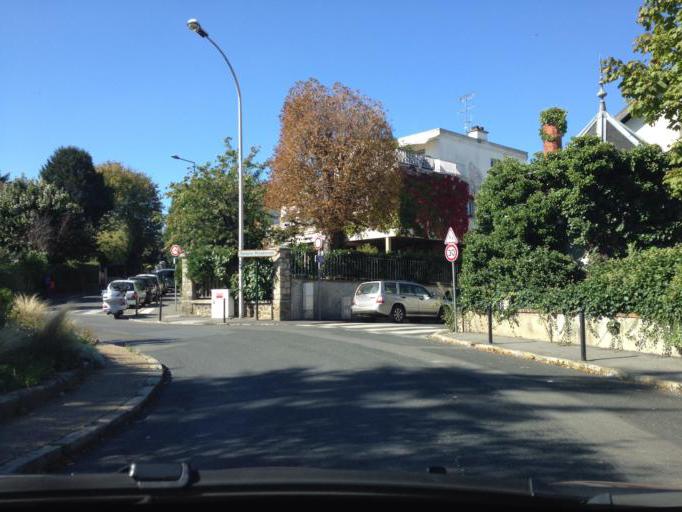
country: FR
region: Ile-de-France
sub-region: Departement des Hauts-de-Seine
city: Sevres
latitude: 48.8196
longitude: 2.2241
